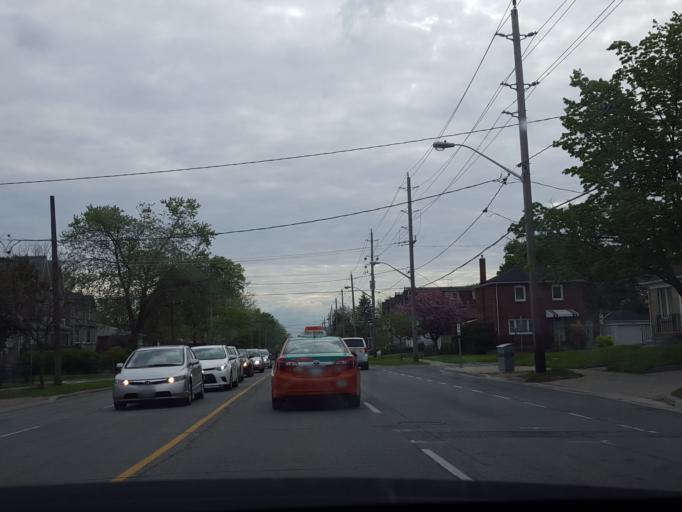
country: CA
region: Ontario
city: Willowdale
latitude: 43.7820
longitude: -79.4053
